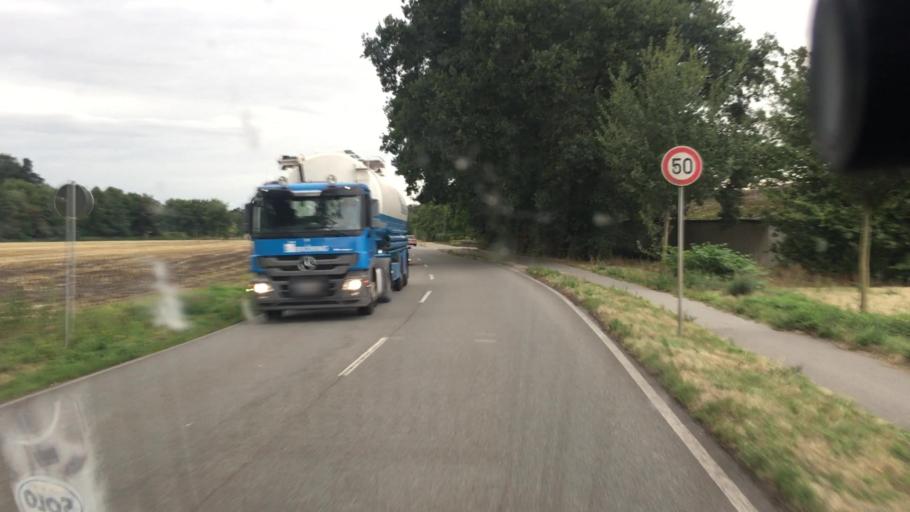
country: DE
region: Lower Saxony
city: Lohne
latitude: 52.6506
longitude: 8.2376
